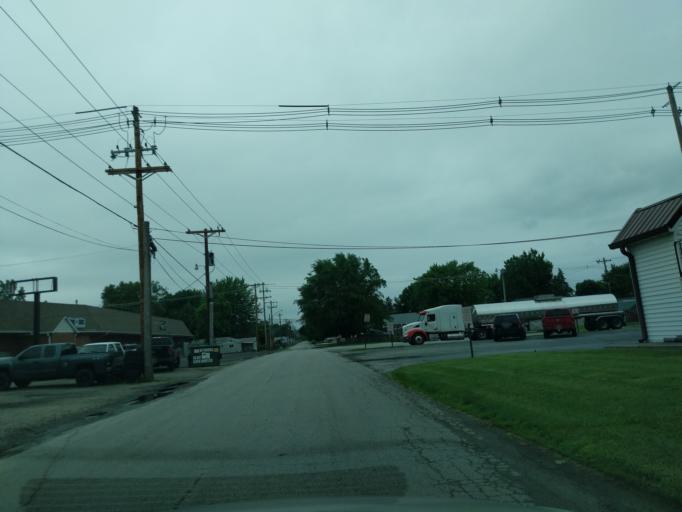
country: US
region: Indiana
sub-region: Tipton County
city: Tipton
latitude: 40.2823
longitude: -86.0498
